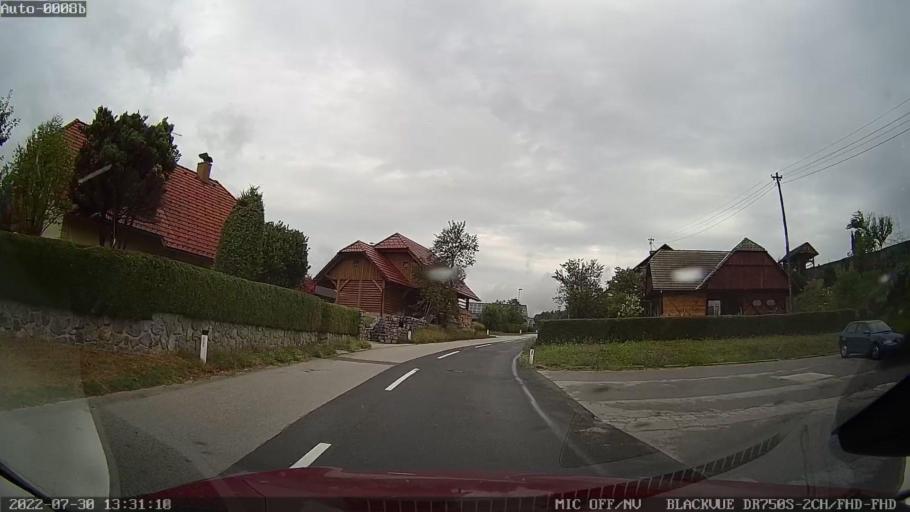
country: SI
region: Zuzemberk
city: Zuzemberk
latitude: 45.8352
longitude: 14.9348
